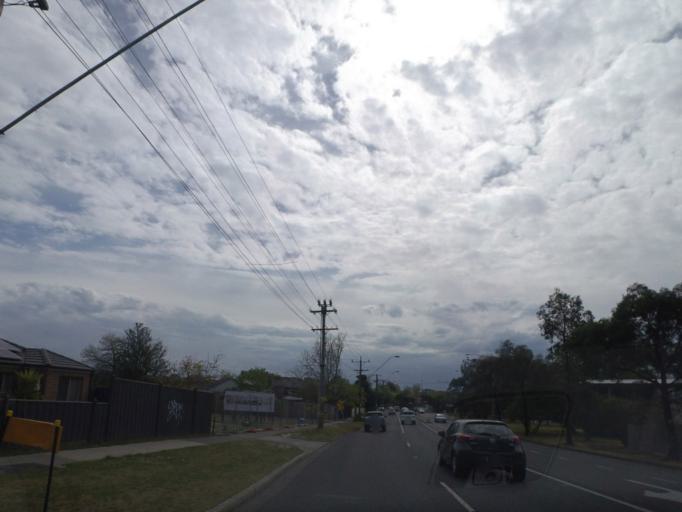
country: AU
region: Victoria
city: Ashburton
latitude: -37.8656
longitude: 145.0916
